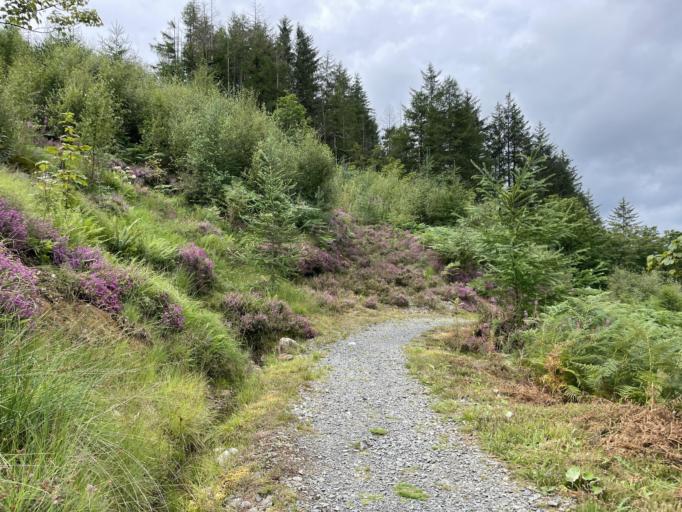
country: GB
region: Scotland
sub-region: Dumfries and Galloway
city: Newton Stewart
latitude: 55.0865
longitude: -4.4819
